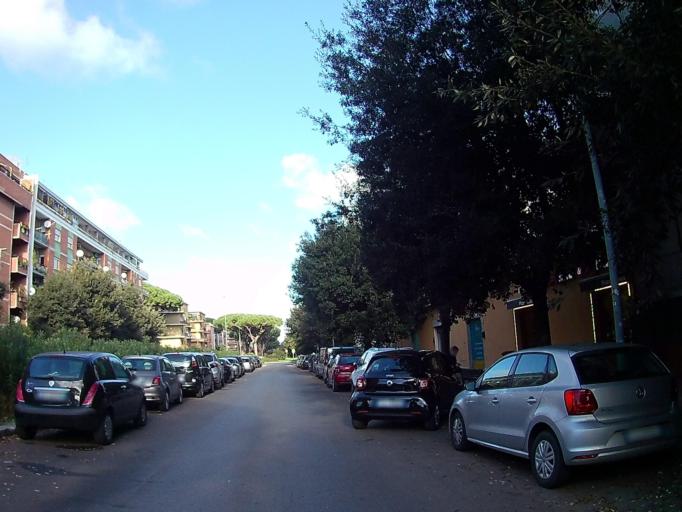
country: IT
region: Latium
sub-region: Citta metropolitana di Roma Capitale
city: Lido di Ostia
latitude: 41.7339
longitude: 12.2908
